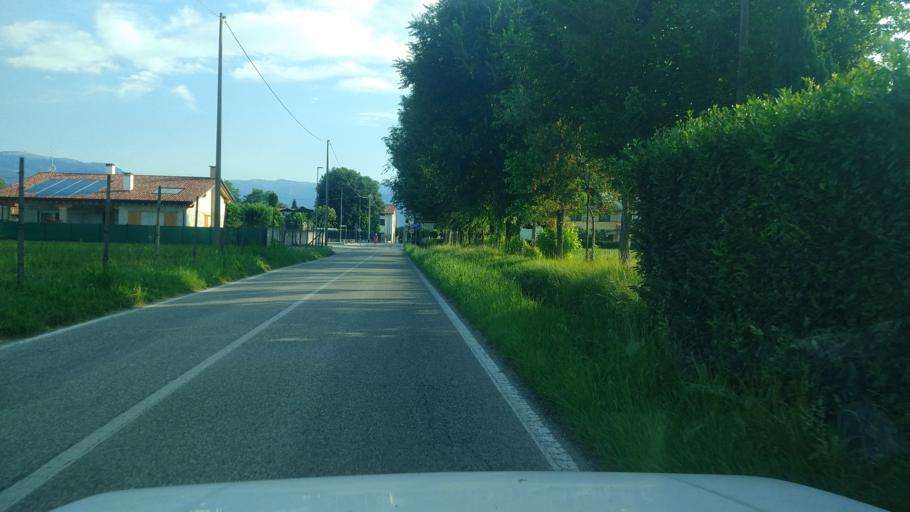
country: IT
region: Veneto
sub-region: Provincia di Vicenza
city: Cartigliano
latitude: 45.7277
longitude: 11.7231
